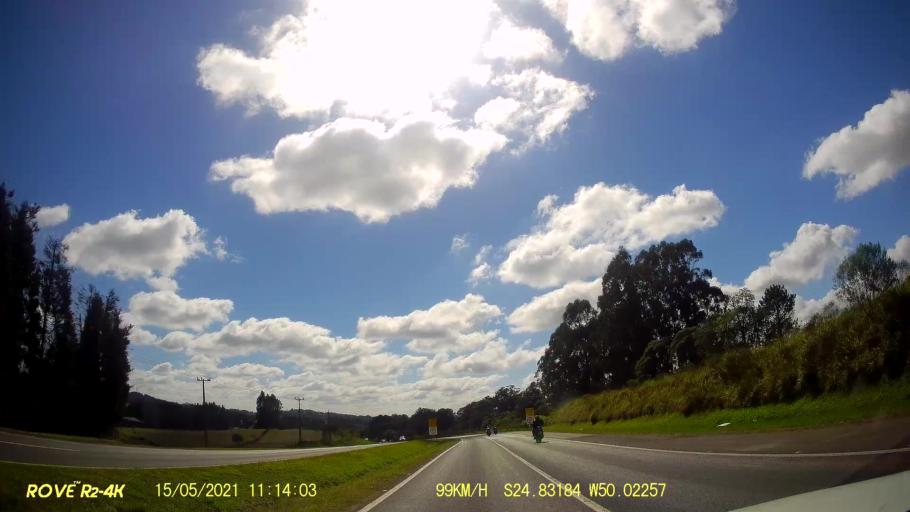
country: BR
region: Parana
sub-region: Castro
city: Castro
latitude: -24.8320
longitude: -50.0225
